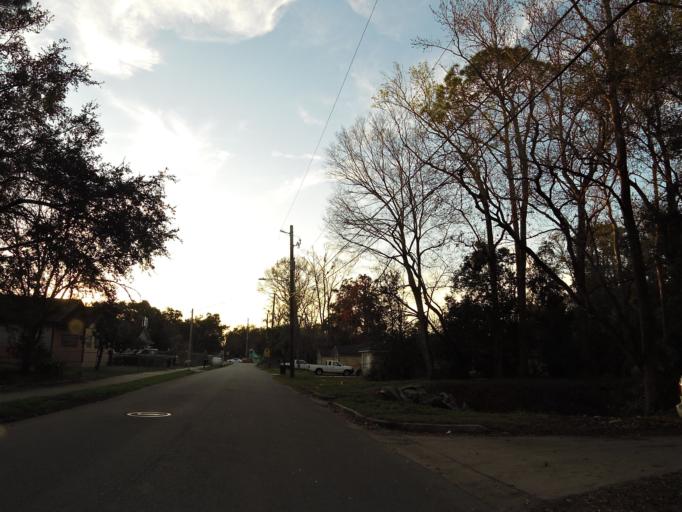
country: US
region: Florida
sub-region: Duval County
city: Jacksonville
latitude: 30.2809
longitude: -81.6419
